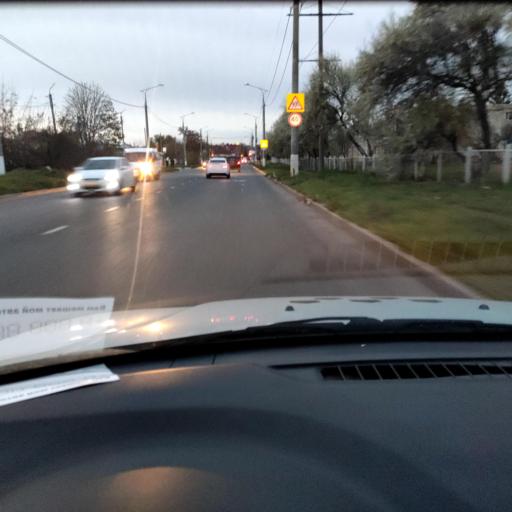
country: RU
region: Samara
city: Tol'yatti
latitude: 53.5122
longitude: 49.3952
